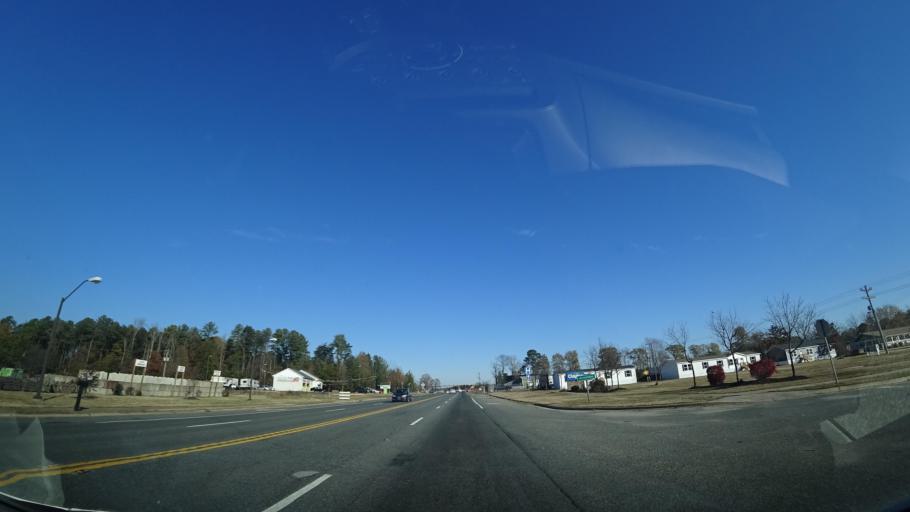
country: US
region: Virginia
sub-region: Spotsylvania County
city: Spotsylvania Courthouse
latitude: 38.1902
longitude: -77.5105
